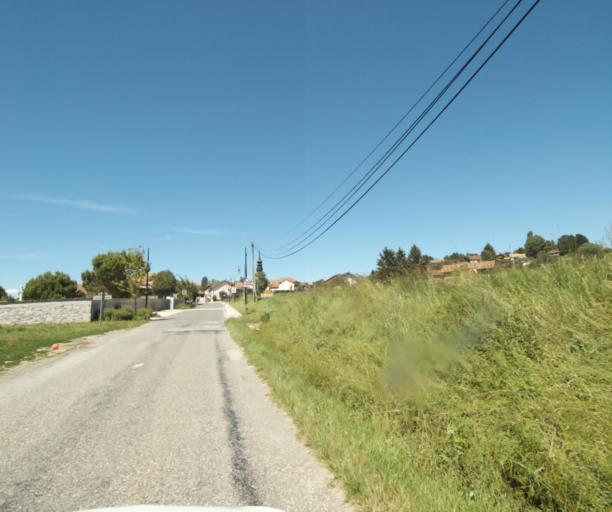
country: FR
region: Rhone-Alpes
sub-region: Departement de la Haute-Savoie
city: Ballaison
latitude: 46.2973
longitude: 6.3272
